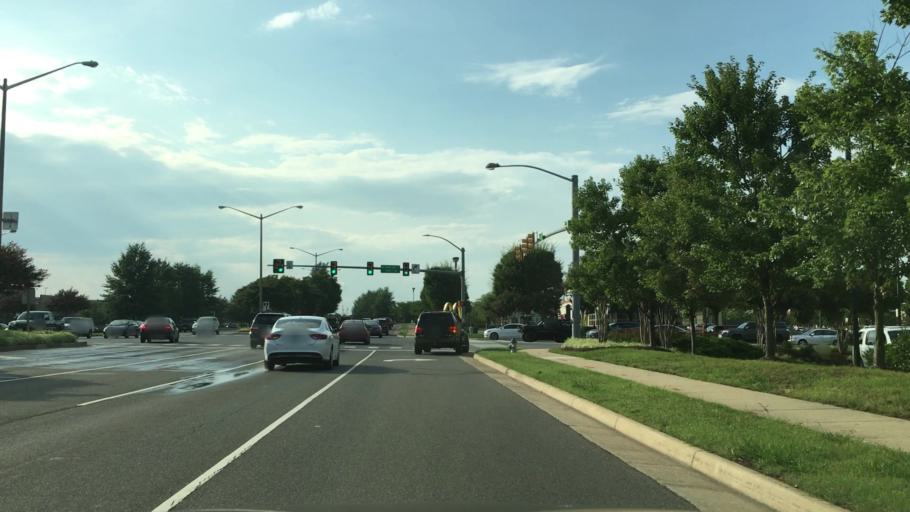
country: US
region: Virginia
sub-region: Stafford County
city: Falmouth
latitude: 38.3049
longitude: -77.5088
